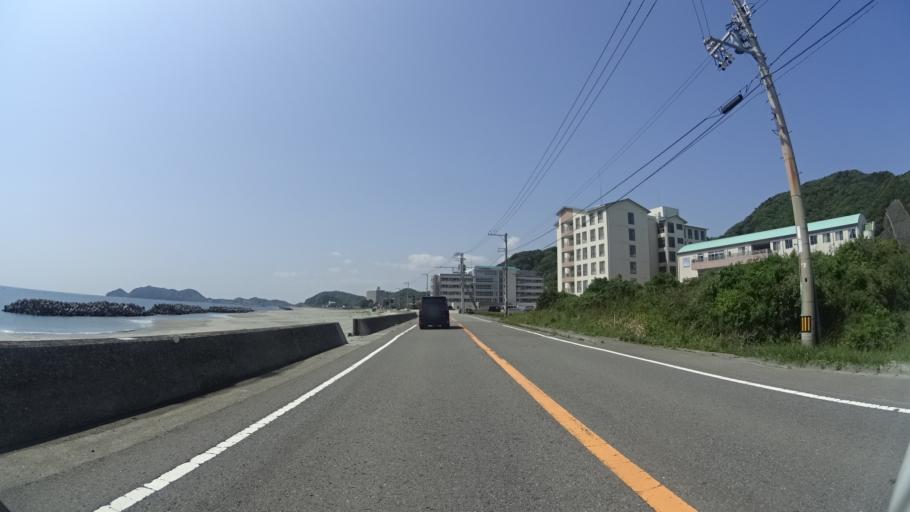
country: JP
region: Tokushima
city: Narutocho-mitsuishi
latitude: 34.2073
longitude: 134.6269
